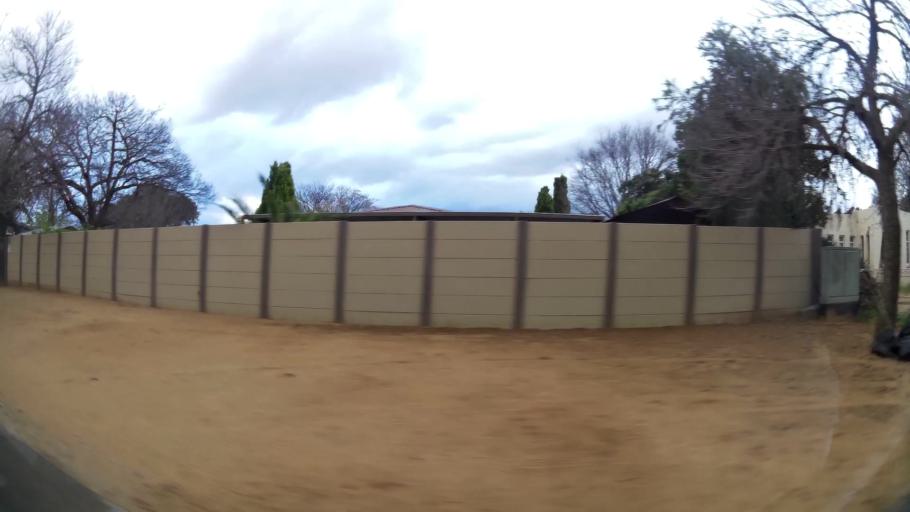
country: ZA
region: Orange Free State
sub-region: Lejweleputswa District Municipality
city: Welkom
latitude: -27.9647
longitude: 26.7241
